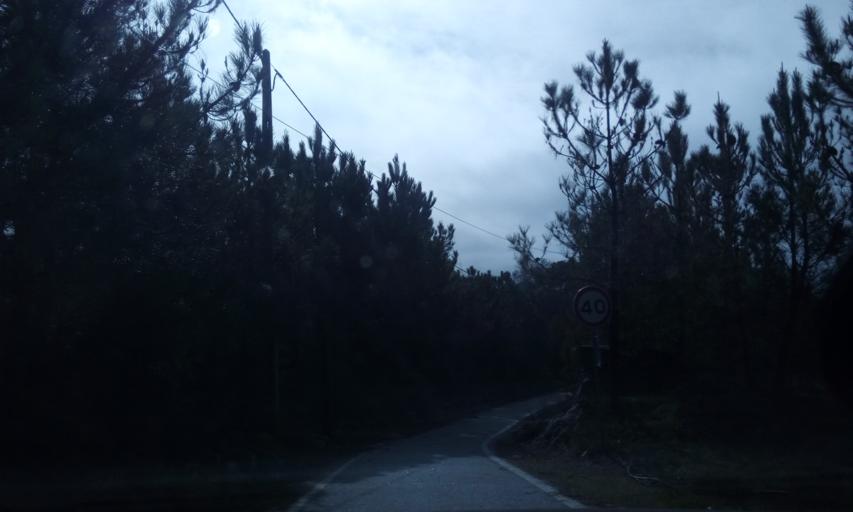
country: PT
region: Guarda
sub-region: Fornos de Algodres
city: Fornos de Algodres
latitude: 40.6362
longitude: -7.5384
